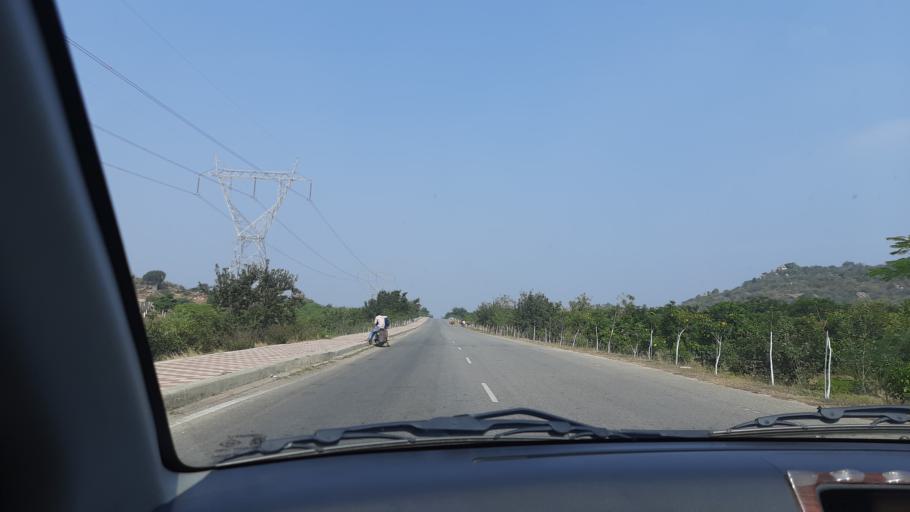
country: IN
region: Telangana
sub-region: Rangareddi
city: Lal Bahadur Nagar
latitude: 17.2864
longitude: 78.6504
